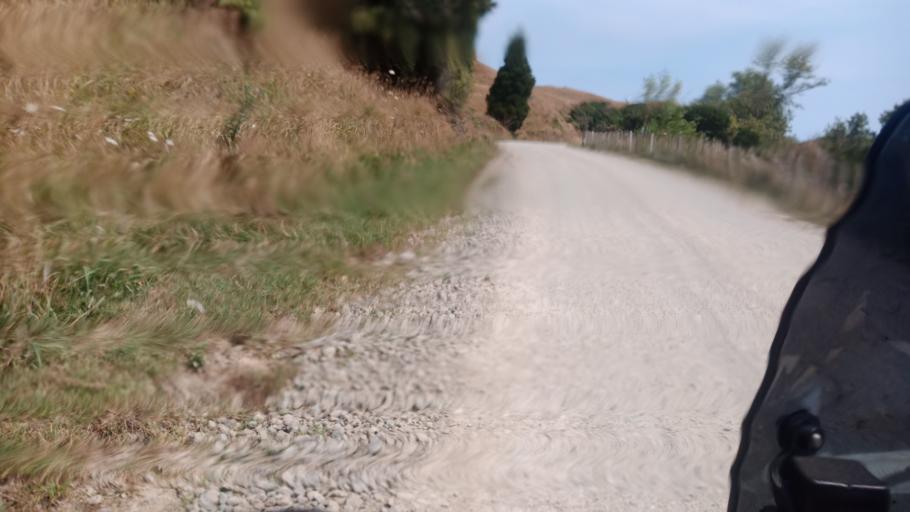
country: NZ
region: Bay of Plenty
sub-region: Opotiki District
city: Opotiki
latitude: -37.6553
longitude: 178.1331
